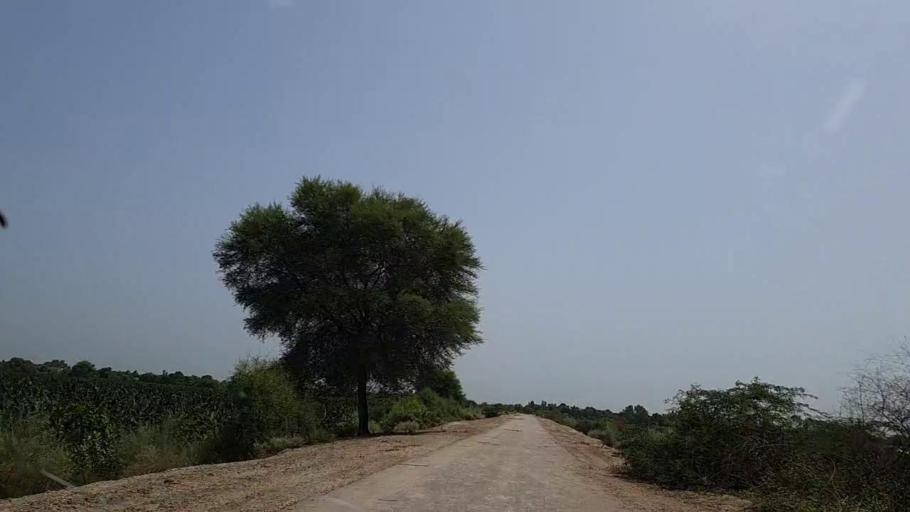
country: PK
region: Sindh
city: Kandiaro
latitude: 27.0541
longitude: 68.1352
